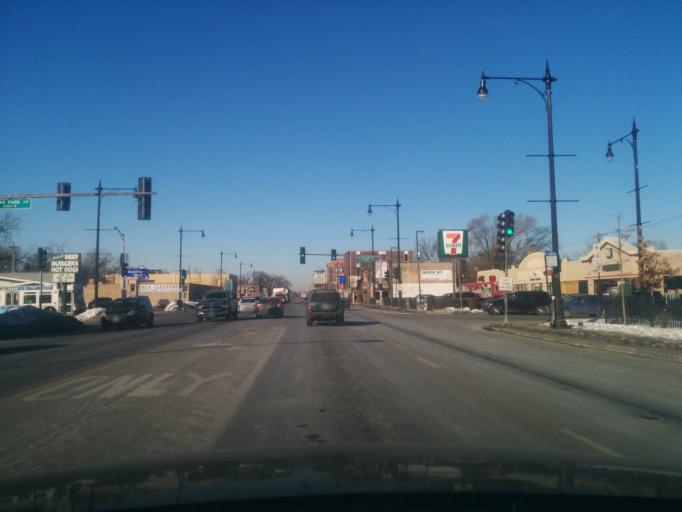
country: US
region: Illinois
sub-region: Cook County
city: Elmwood Park
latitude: 41.9090
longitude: -87.7942
